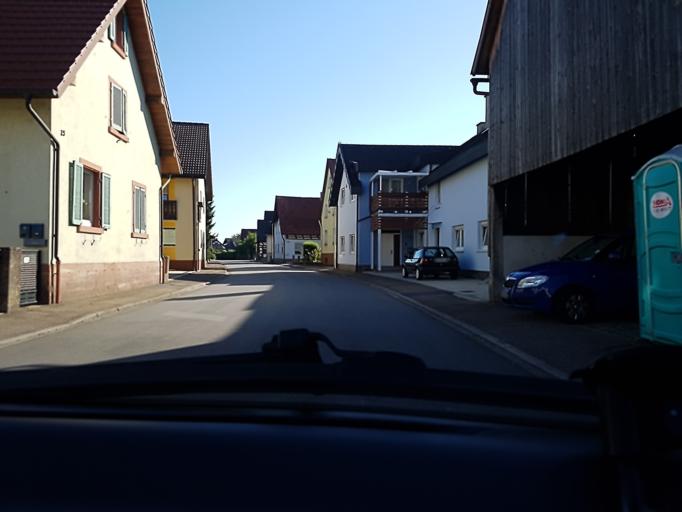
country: DE
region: Baden-Wuerttemberg
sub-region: Freiburg Region
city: Willstatt
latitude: 48.5733
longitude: 7.9136
